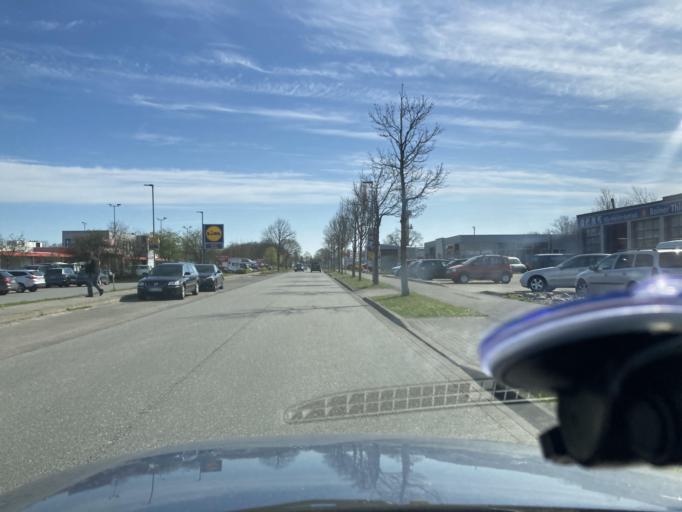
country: DE
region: Schleswig-Holstein
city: Ostrohe
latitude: 54.1963
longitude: 9.1316
